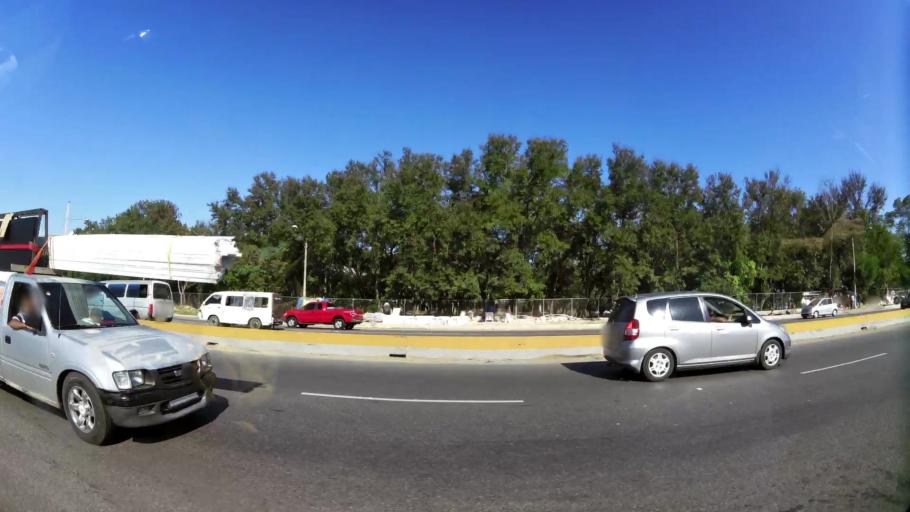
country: DO
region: Nacional
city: Bella Vista
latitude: 18.4761
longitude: -69.9679
